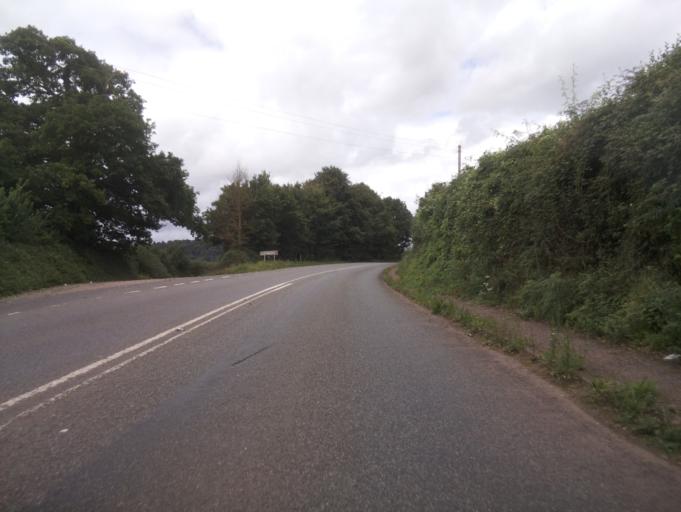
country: GB
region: England
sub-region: Devon
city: Bradninch
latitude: 50.7815
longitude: -3.4417
